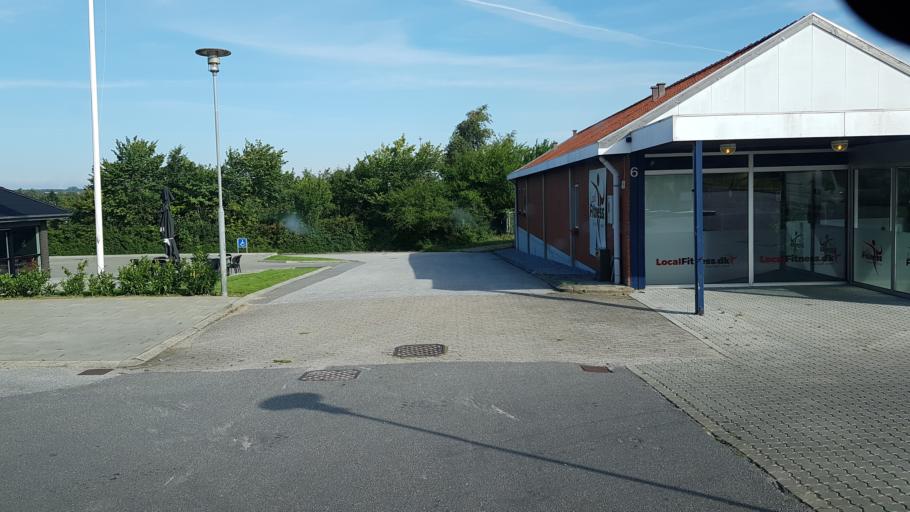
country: DK
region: South Denmark
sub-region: Haderslev Kommune
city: Starup
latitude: 55.2429
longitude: 9.5367
